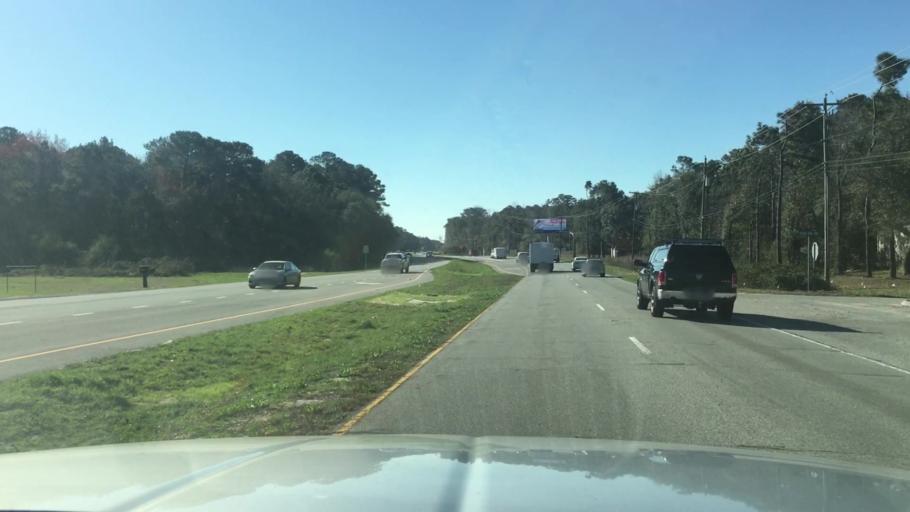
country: US
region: North Carolina
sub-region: New Hanover County
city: Sea Breeze
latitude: 34.0998
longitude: -77.8992
